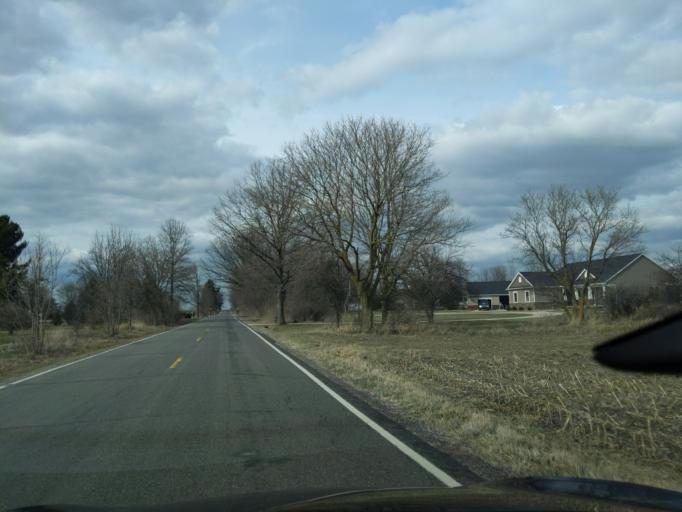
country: US
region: Michigan
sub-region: Ingham County
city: Mason
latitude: 42.5476
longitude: -84.4832
